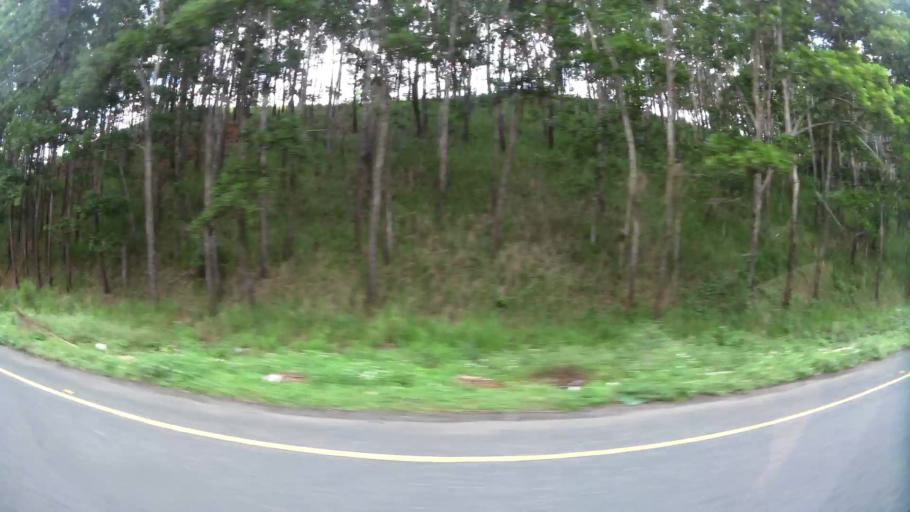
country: DO
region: Monsenor Nouel
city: Piedra Blanca
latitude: 18.8209
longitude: -70.2899
